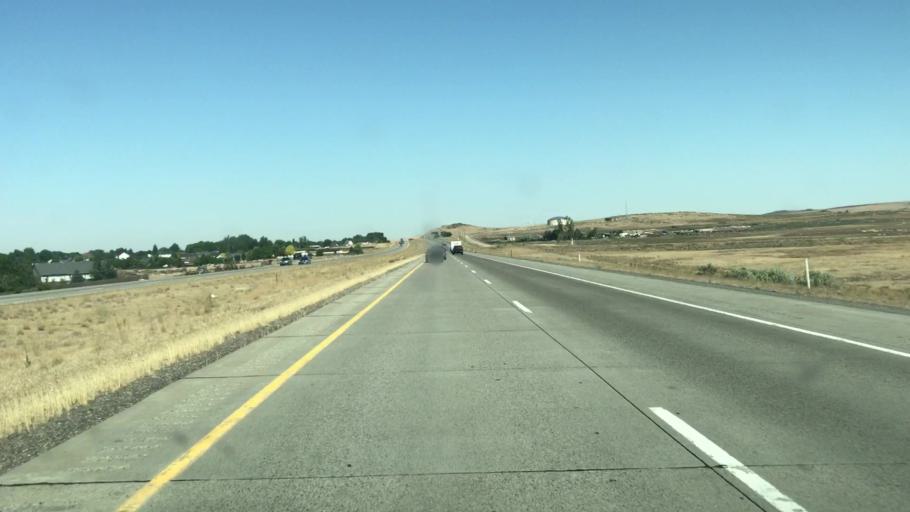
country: US
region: Idaho
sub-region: Elmore County
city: Mountain Home
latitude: 43.1543
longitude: -115.6848
